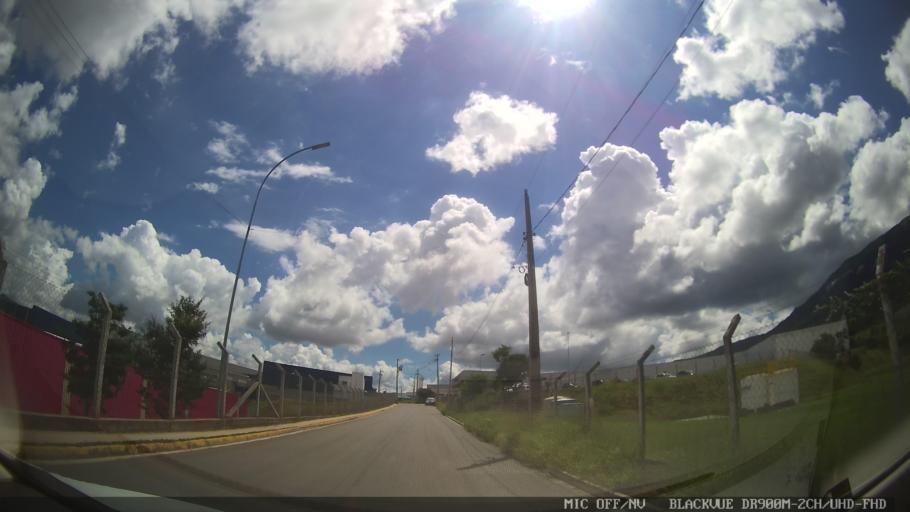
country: BR
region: Minas Gerais
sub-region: Extrema
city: Extrema
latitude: -22.8781
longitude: -46.3512
